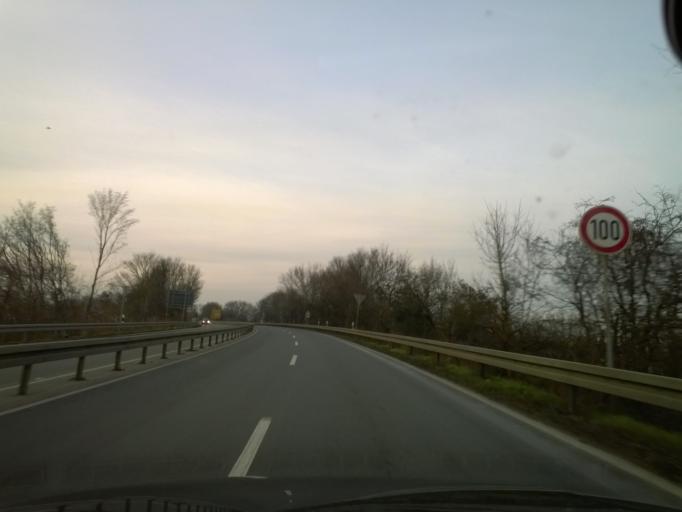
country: DE
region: Lower Saxony
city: Hildesheim
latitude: 52.1606
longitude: 9.9716
